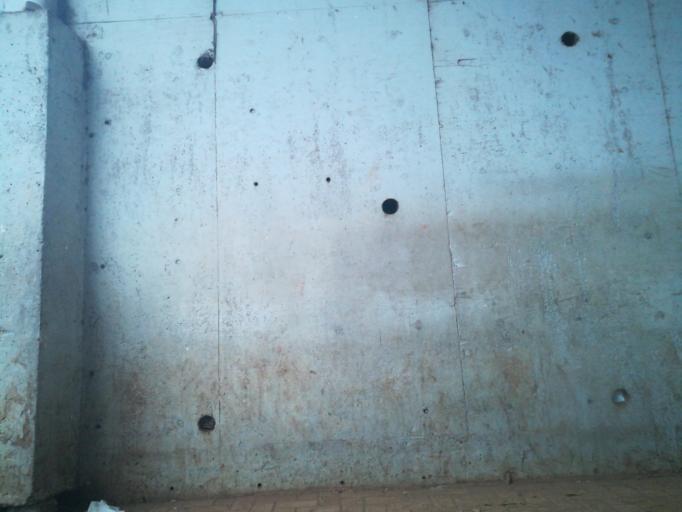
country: KE
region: Nairobi Area
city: Thika
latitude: -1.1331
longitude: 36.9743
